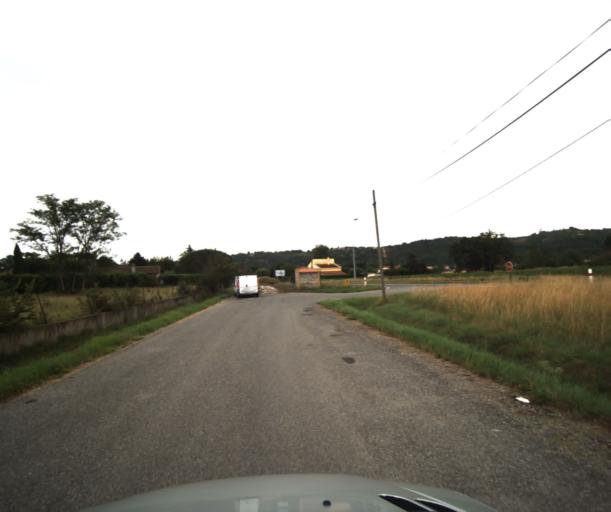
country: FR
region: Midi-Pyrenees
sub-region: Departement de la Haute-Garonne
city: Lacroix-Falgarde
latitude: 43.4897
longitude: 1.3997
